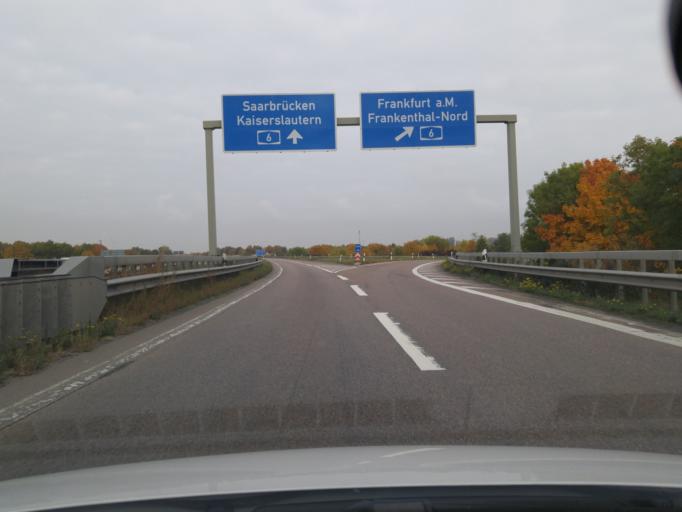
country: DE
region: Rheinland-Pfalz
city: Hessheim
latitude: 49.5506
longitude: 8.3150
